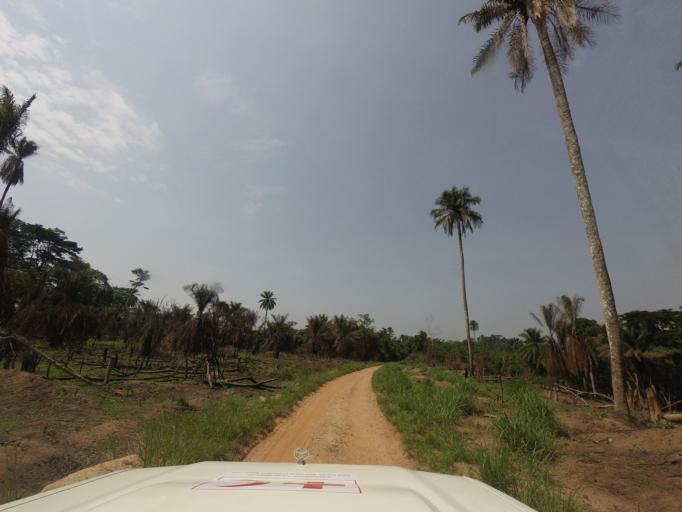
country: LR
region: Lofa
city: Voinjama
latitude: 8.5096
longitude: -9.6332
